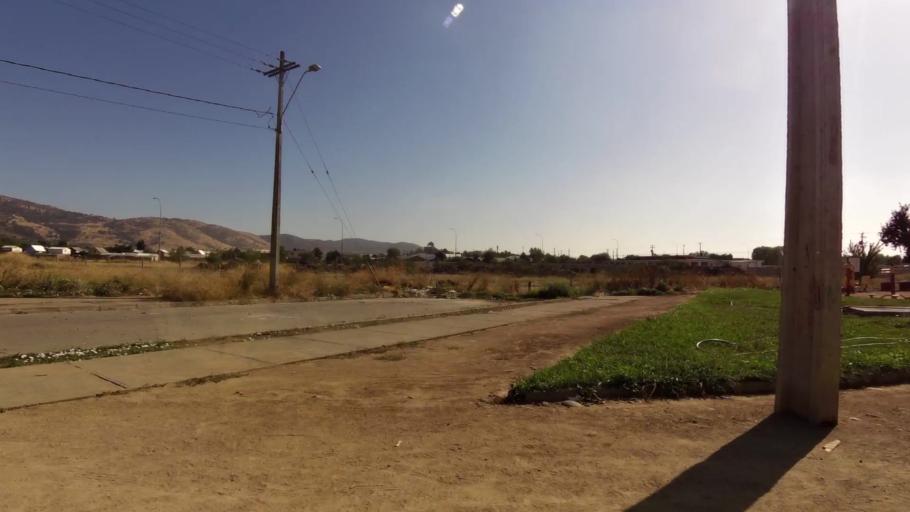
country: CL
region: Maule
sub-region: Provincia de Talca
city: Talca
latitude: -35.3983
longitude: -71.6530
